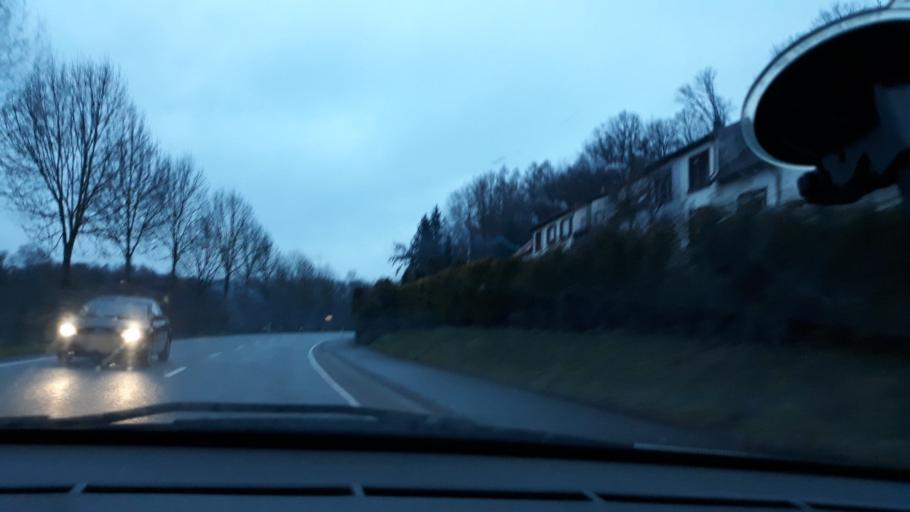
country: DE
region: Saarland
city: Blieskastel
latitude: 49.2040
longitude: 7.2464
